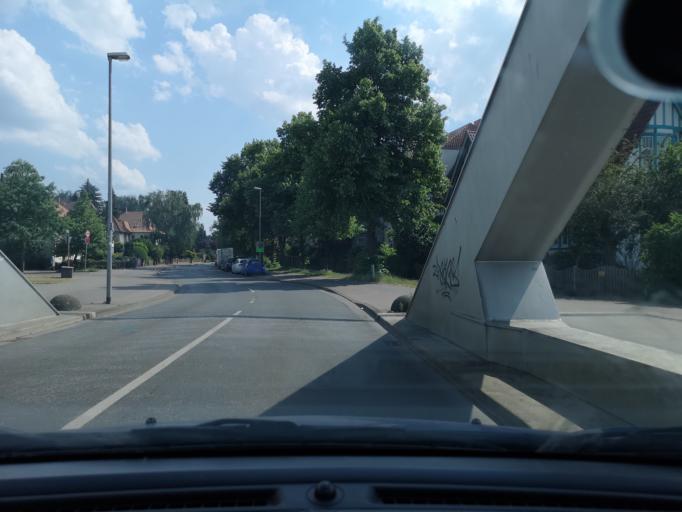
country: DE
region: Lower Saxony
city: Hannover
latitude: 52.4052
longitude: 9.8007
